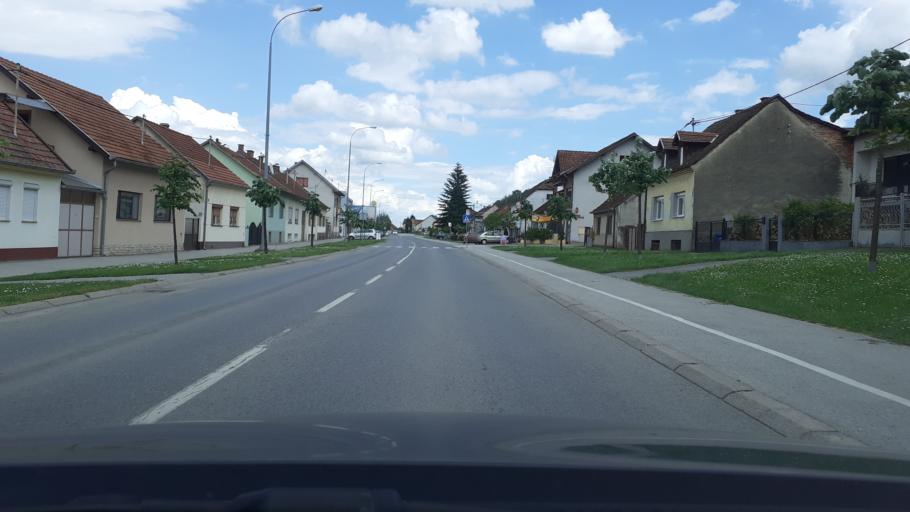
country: HR
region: Pozesko-Slavonska
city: Pozega
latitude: 45.3339
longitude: 17.6958
